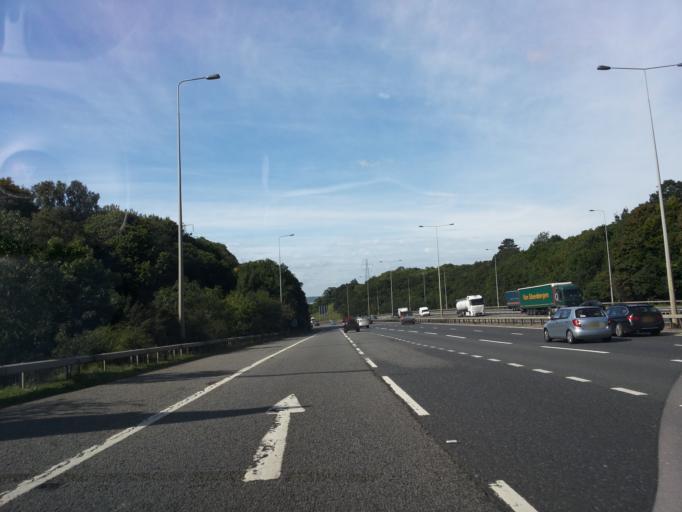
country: GB
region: England
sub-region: Kent
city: Boxley
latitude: 51.2887
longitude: 0.5446
